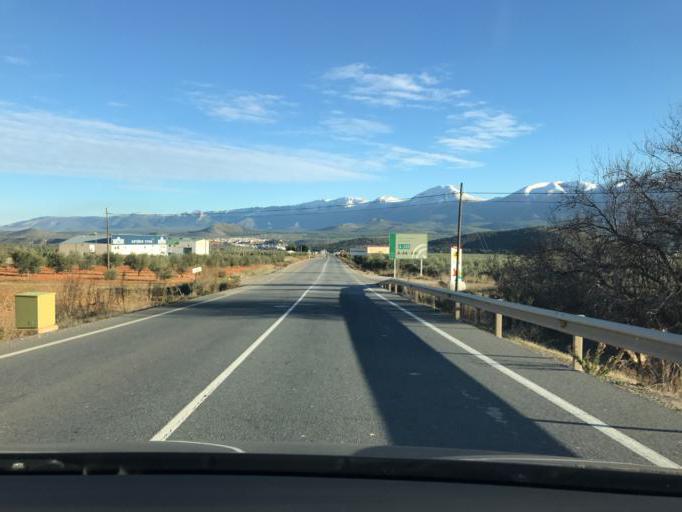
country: ES
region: Andalusia
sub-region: Provincia de Granada
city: Iznalloz
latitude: 37.4042
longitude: -3.5613
